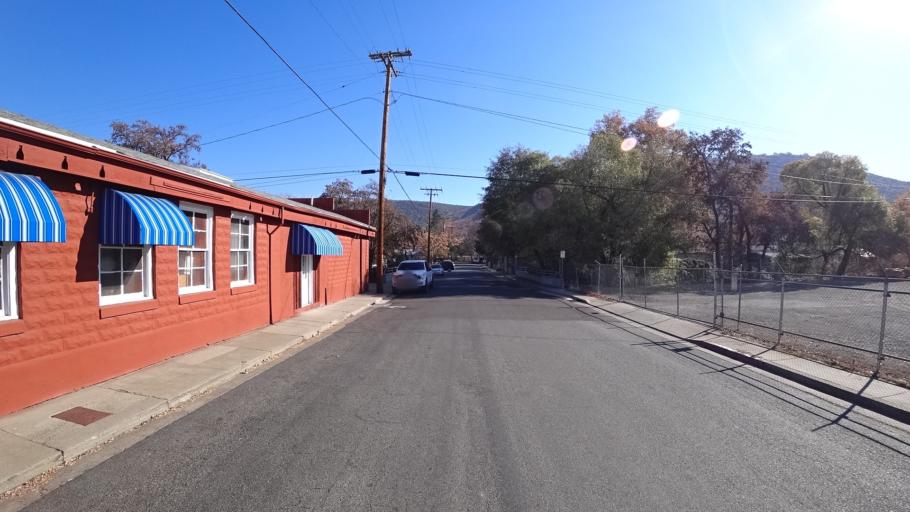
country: US
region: California
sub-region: Siskiyou County
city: Yreka
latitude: 41.7287
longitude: -122.6363
